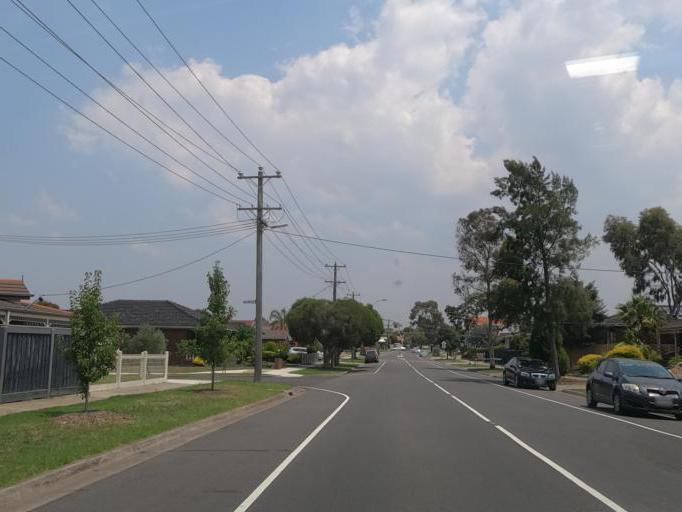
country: AU
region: Victoria
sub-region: Hume
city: Greenvale
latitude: -37.6426
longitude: 144.8901
